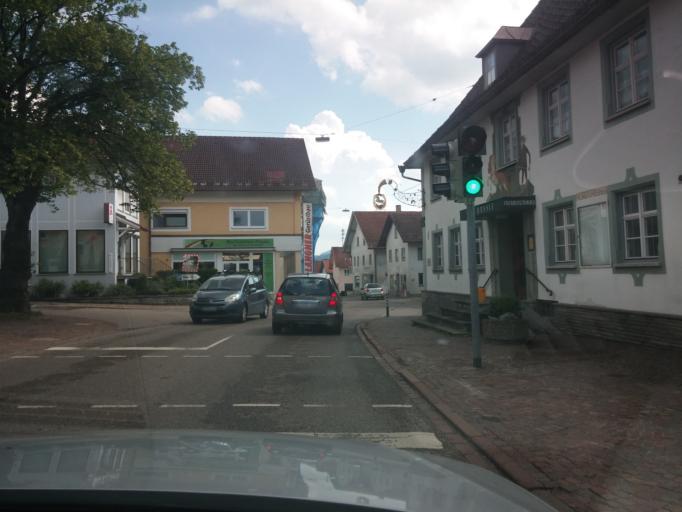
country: DE
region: Bavaria
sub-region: Swabia
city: Altusried
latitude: 47.8046
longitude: 10.2146
